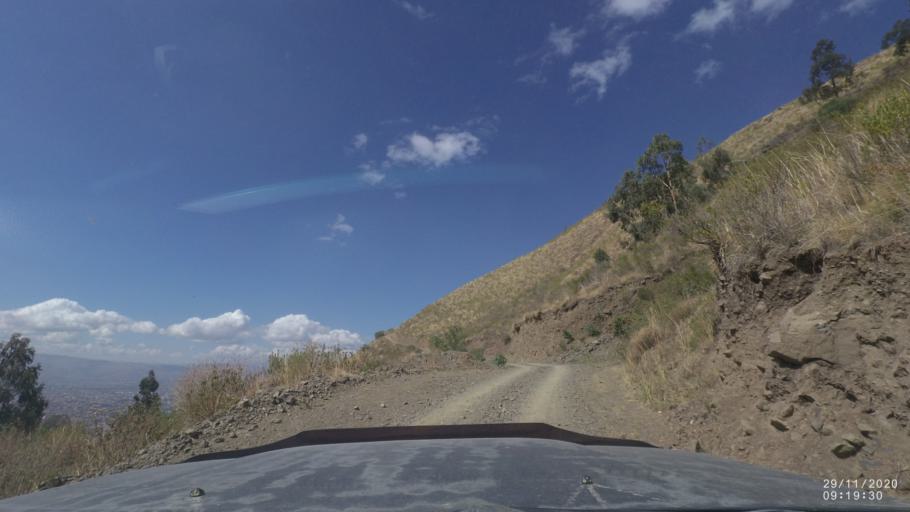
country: BO
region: Cochabamba
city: Cochabamba
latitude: -17.3221
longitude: -66.1834
